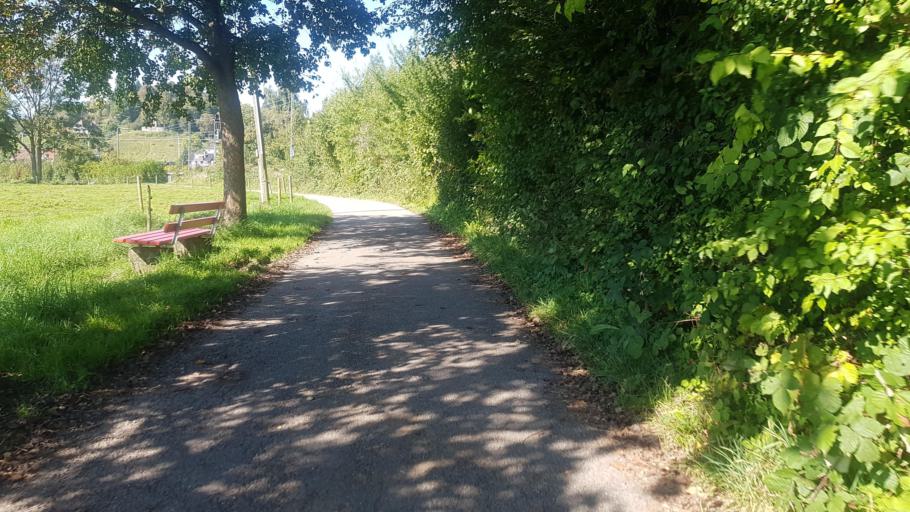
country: DE
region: Bavaria
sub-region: Swabia
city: Bodolz
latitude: 47.5620
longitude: 9.6813
